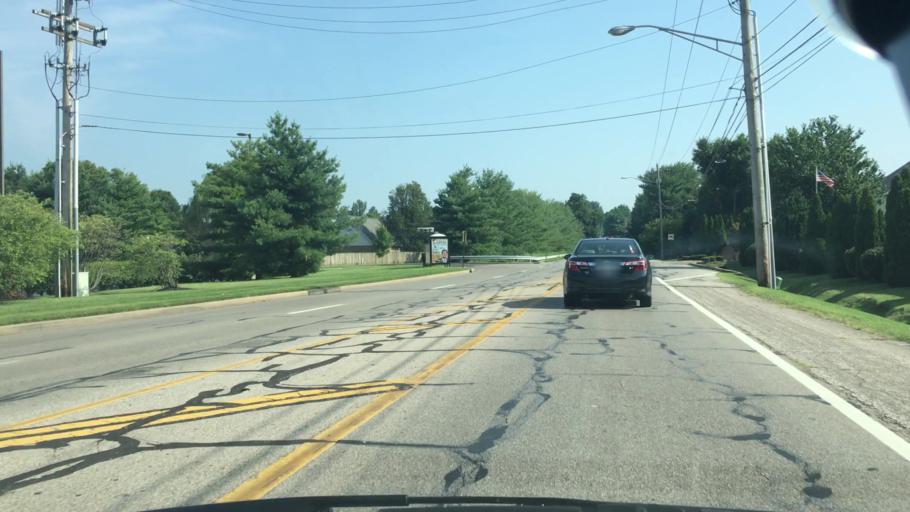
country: US
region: Indiana
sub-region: Vanderburgh County
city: Melody Hill
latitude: 37.9738
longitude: -87.4743
